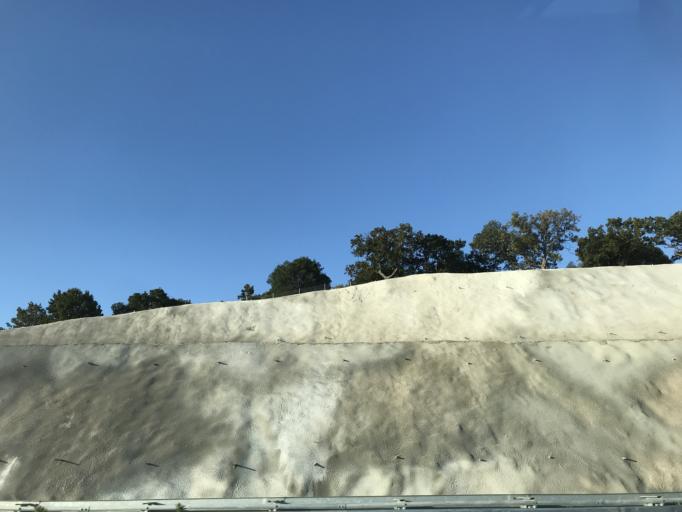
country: TR
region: Bursa
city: Mahmudiye
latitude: 40.2609
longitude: 28.6780
